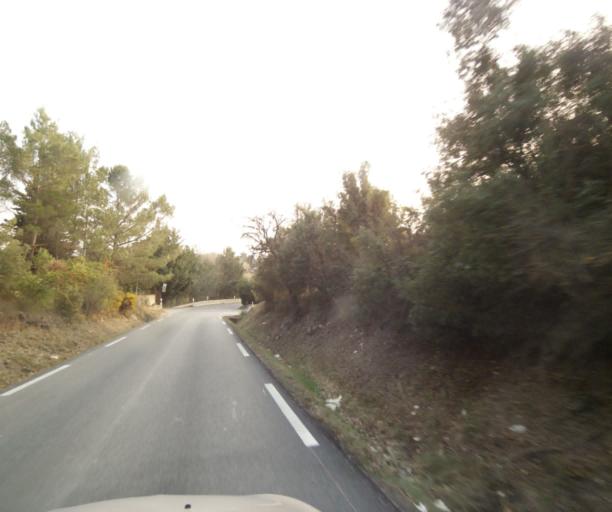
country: FR
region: Provence-Alpes-Cote d'Azur
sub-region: Departement des Bouches-du-Rhone
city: Eguilles
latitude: 43.5843
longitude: 5.3696
